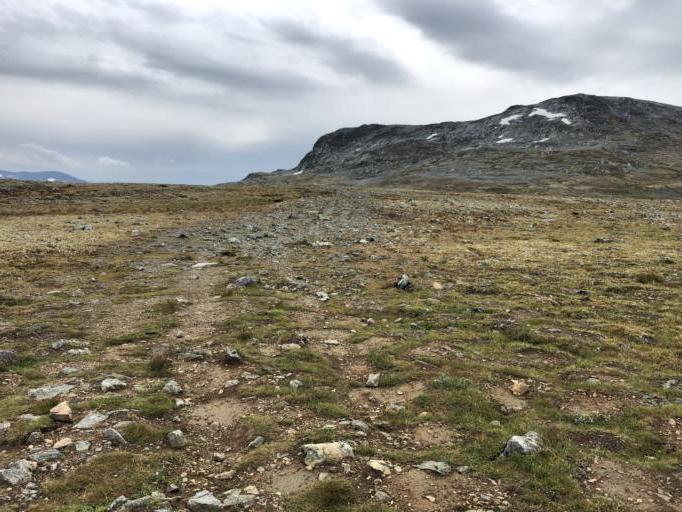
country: NO
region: Oppland
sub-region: Lom
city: Fossbergom
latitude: 61.5239
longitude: 8.8103
